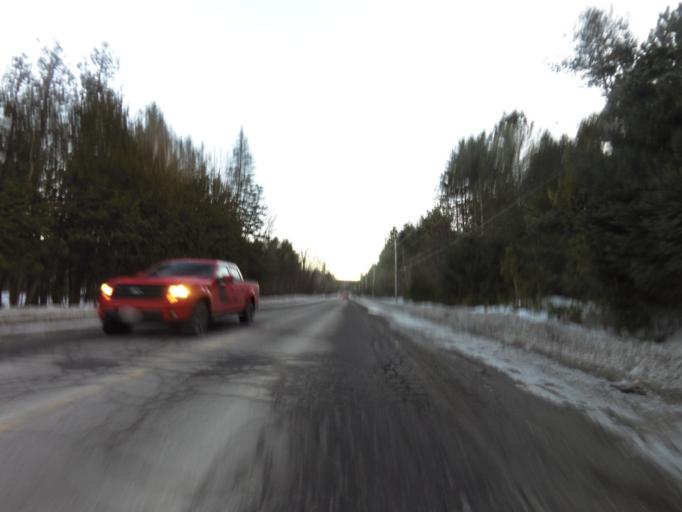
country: CA
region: Quebec
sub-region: Outaouais
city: Gatineau
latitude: 45.4946
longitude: -75.8139
